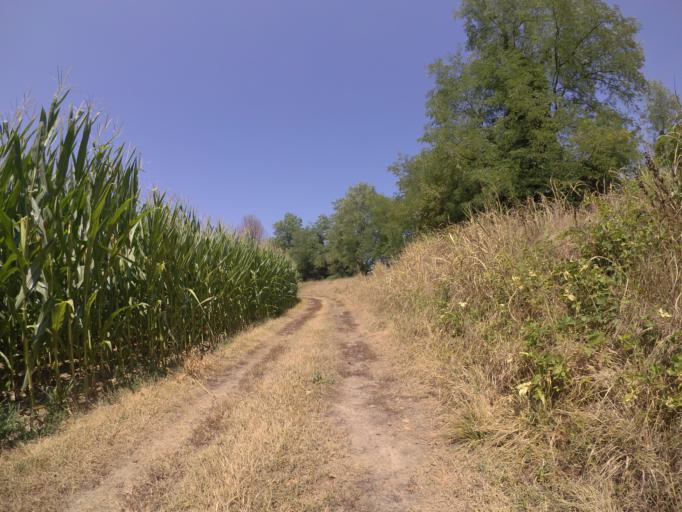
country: IT
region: Friuli Venezia Giulia
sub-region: Provincia di Udine
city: Varmo
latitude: 45.9243
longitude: 13.0136
